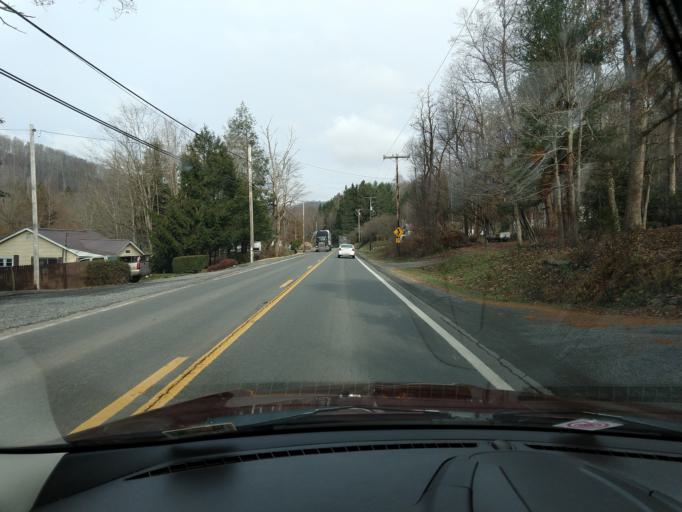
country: US
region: West Virginia
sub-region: Greenbrier County
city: Rainelle
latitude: 37.9935
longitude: -80.7345
